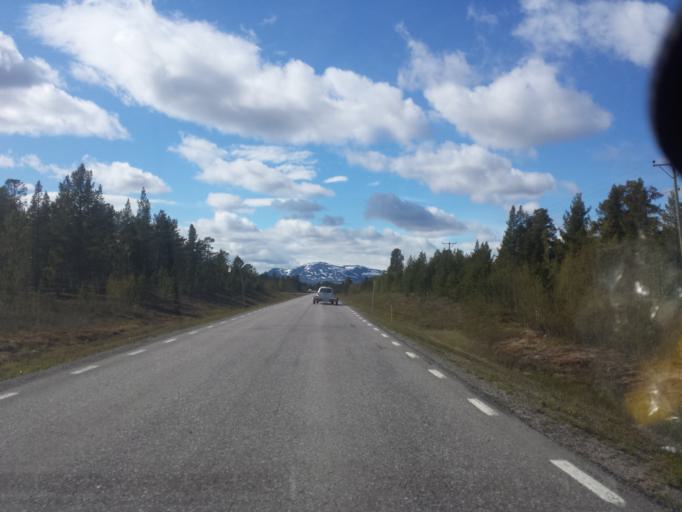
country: SE
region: Norrbotten
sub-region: Kiruna Kommun
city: Kiruna
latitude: 67.9916
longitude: 19.9185
